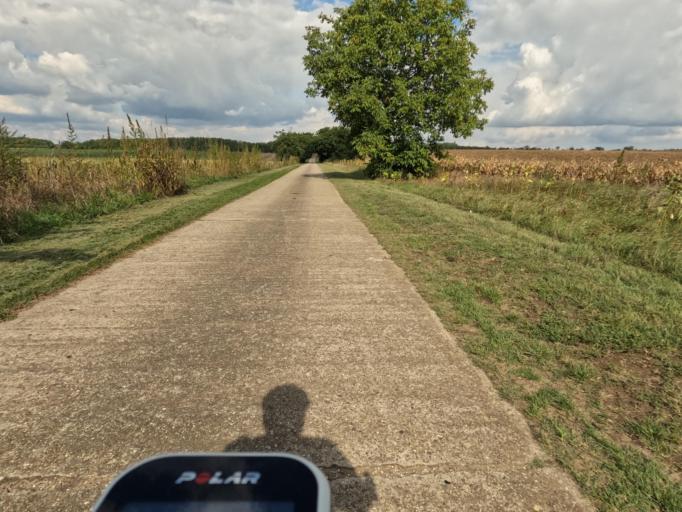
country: HU
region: Tolna
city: Tengelic
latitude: 46.5122
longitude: 18.6918
